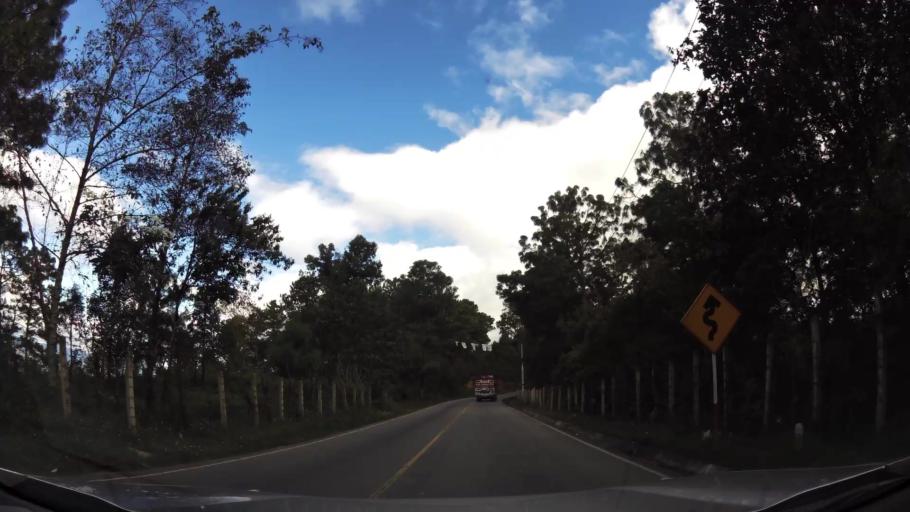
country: GT
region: Quiche
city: Chichicastenango
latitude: 14.9139
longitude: -91.1037
